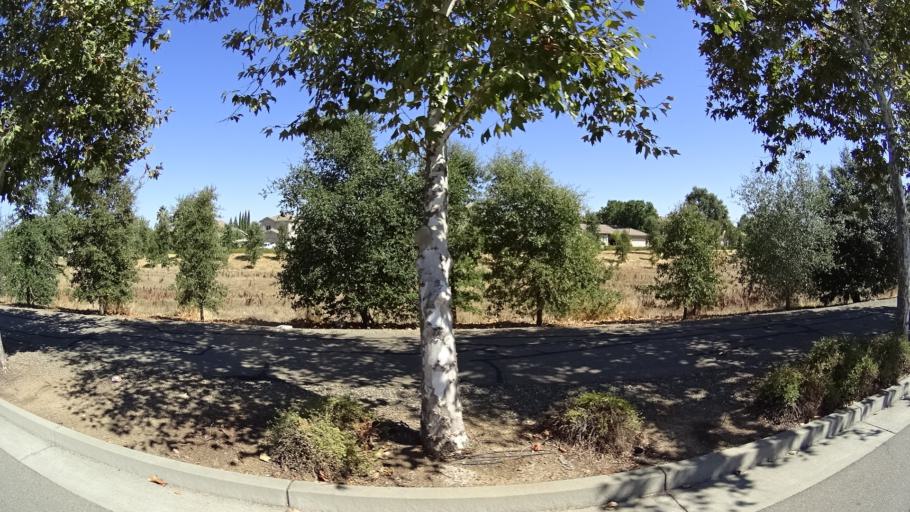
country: US
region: California
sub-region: Sacramento County
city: Elk Grove
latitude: 38.4220
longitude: -121.3478
